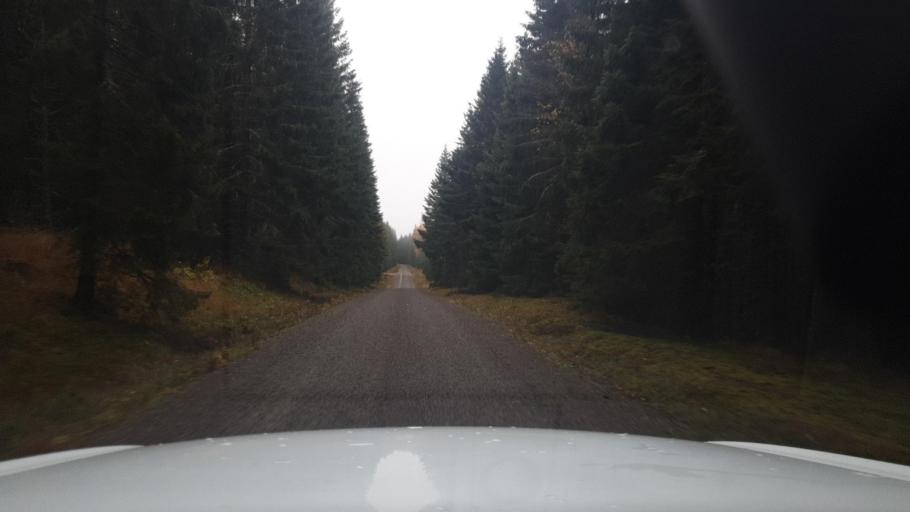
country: SE
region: Vaermland
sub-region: Eda Kommun
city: Charlottenberg
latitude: 60.0373
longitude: 12.6300
